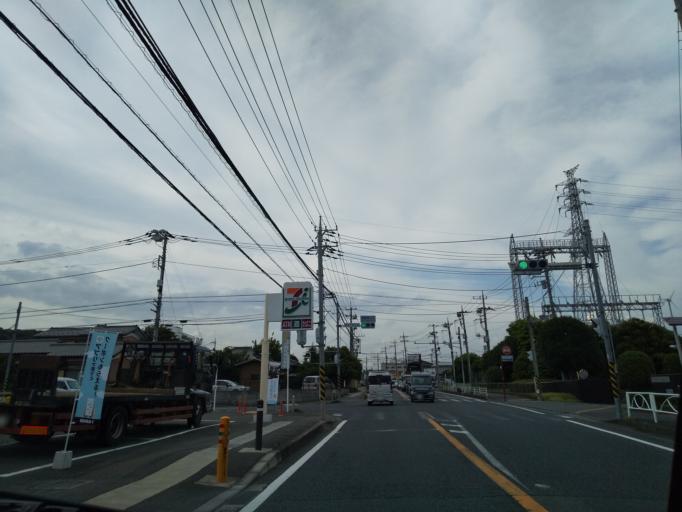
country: JP
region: Kanagawa
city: Zama
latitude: 35.4905
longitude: 139.3400
